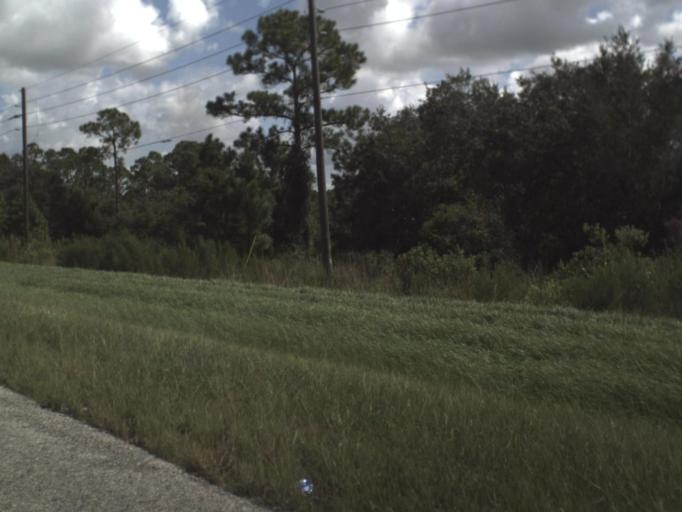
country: US
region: Florida
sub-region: Charlotte County
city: Harbour Heights
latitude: 26.9980
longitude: -81.9588
